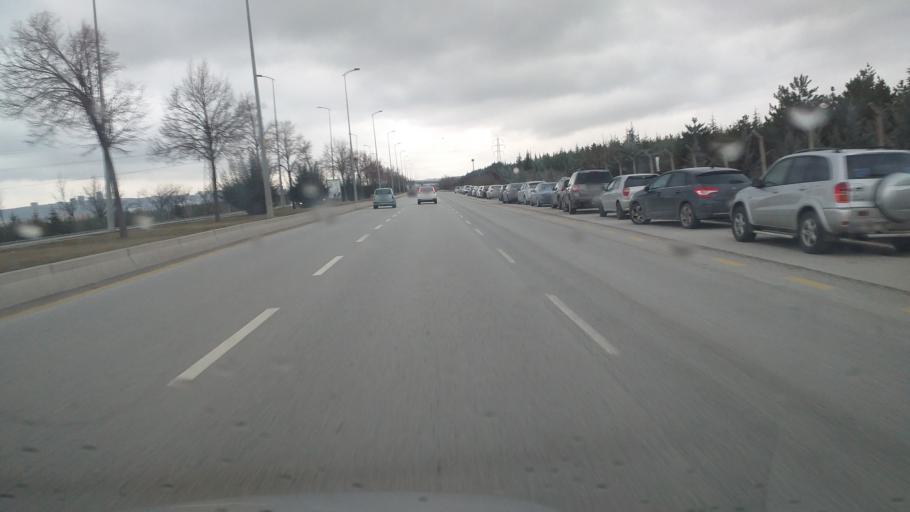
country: TR
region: Ankara
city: Batikent
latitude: 39.9035
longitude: 32.7328
